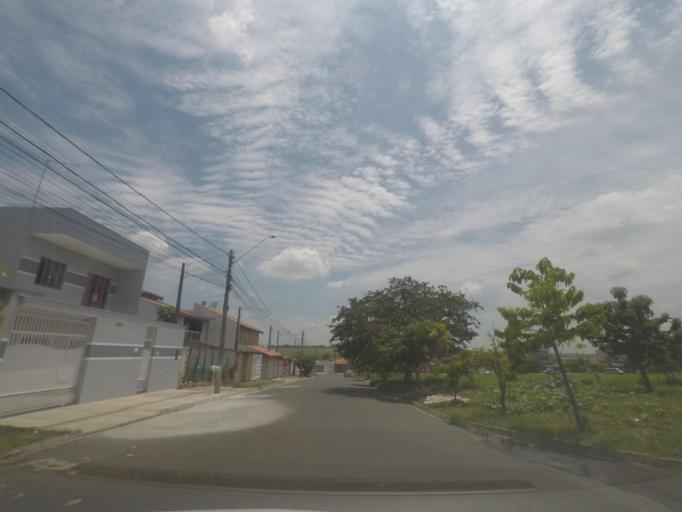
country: BR
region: Sao Paulo
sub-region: Sumare
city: Sumare
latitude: -22.8000
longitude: -47.2739
